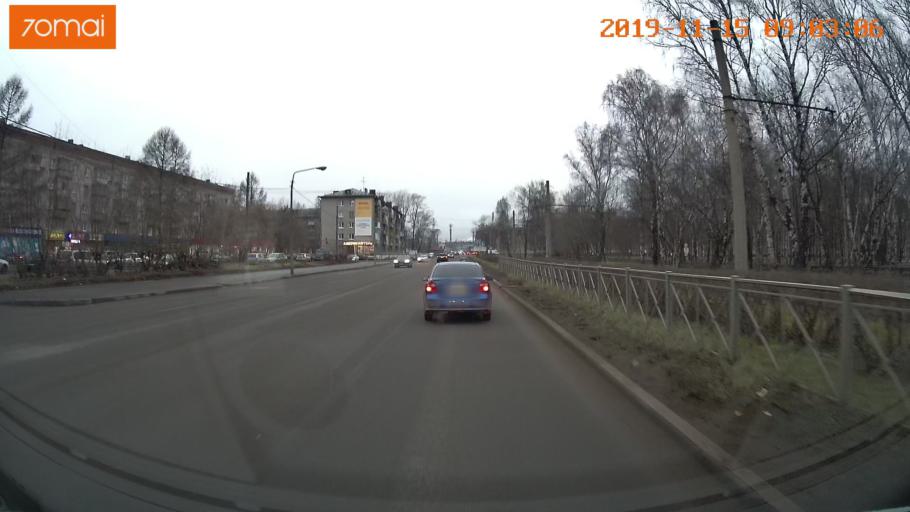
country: RU
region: Vologda
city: Cherepovets
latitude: 59.1374
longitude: 37.9245
